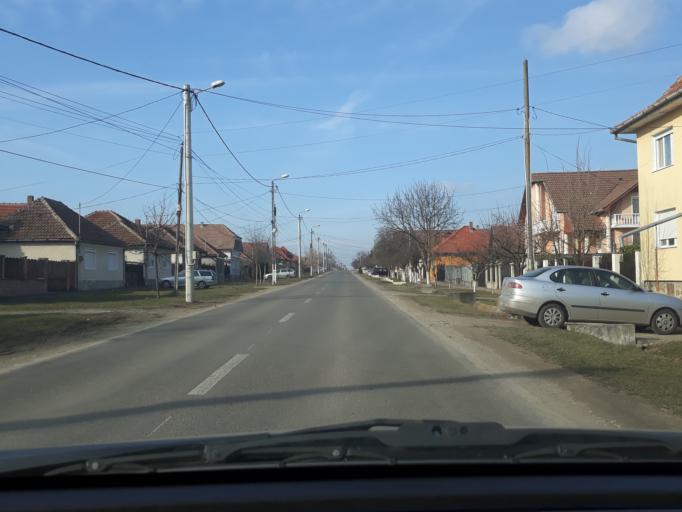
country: RO
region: Bihor
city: Margita
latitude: 47.3546
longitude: 22.3378
